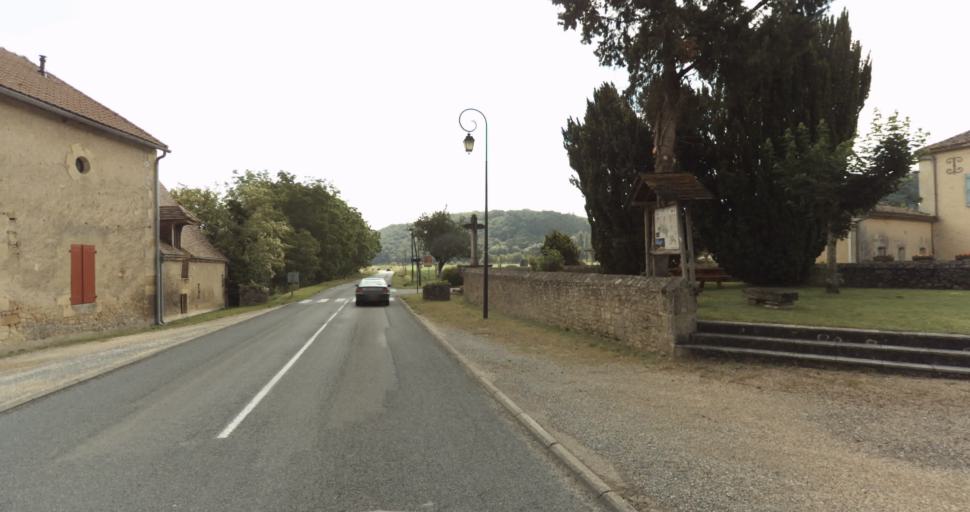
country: FR
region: Aquitaine
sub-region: Departement de la Dordogne
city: Lalinde
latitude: 44.8368
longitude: 0.7630
